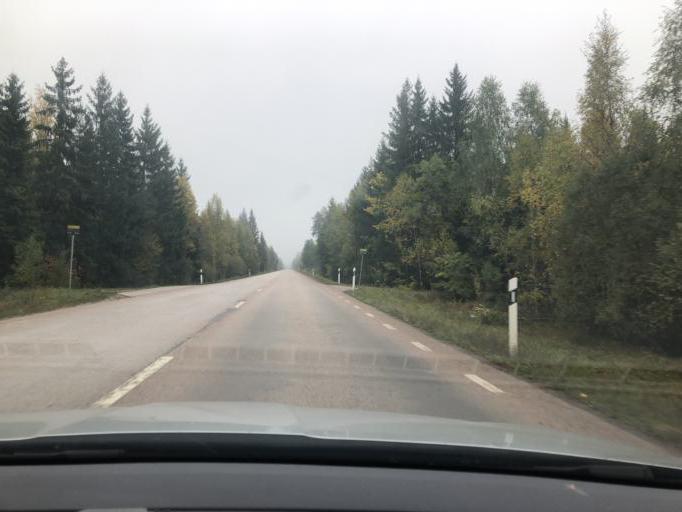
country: SE
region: Uppsala
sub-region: Tierps Kommun
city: Orbyhus
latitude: 60.2155
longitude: 17.7483
